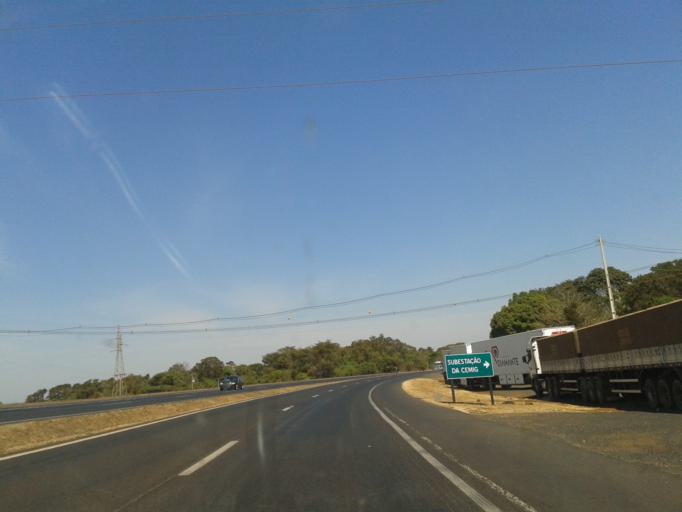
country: BR
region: Minas Gerais
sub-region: Monte Alegre De Minas
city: Monte Alegre de Minas
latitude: -18.7731
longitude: -49.0735
